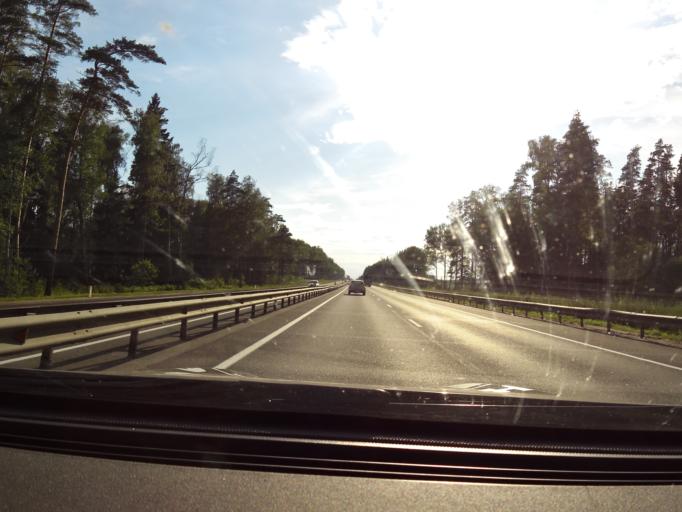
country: RU
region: Vladimir
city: Krasnyy Oktyabr'
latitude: 56.2205
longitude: 41.5060
